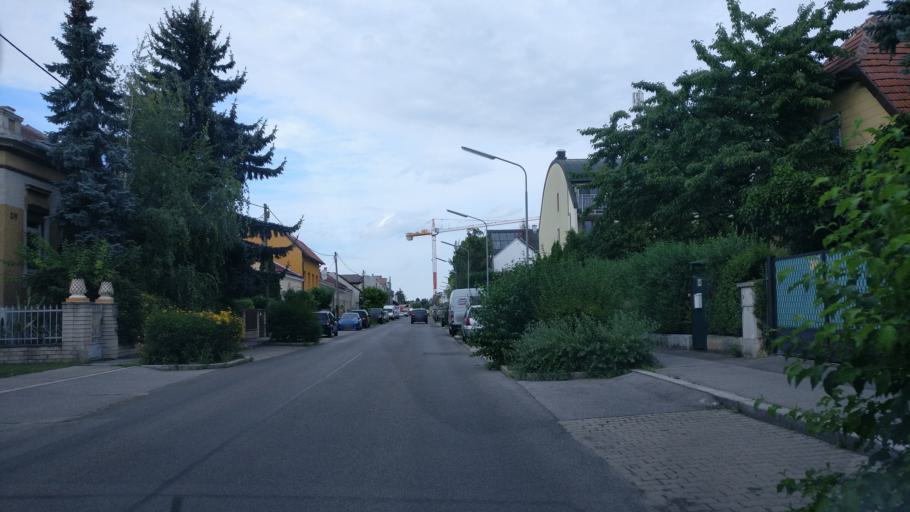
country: AT
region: Lower Austria
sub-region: Politischer Bezirk Korneuburg
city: Hagenbrunn
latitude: 48.2920
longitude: 16.4119
